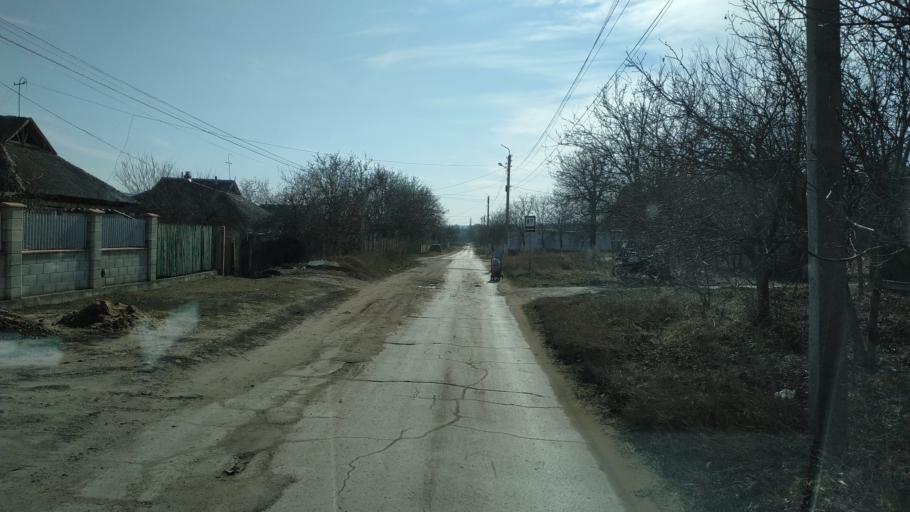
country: MD
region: Nisporeni
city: Nisporeni
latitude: 47.0671
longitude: 28.1735
